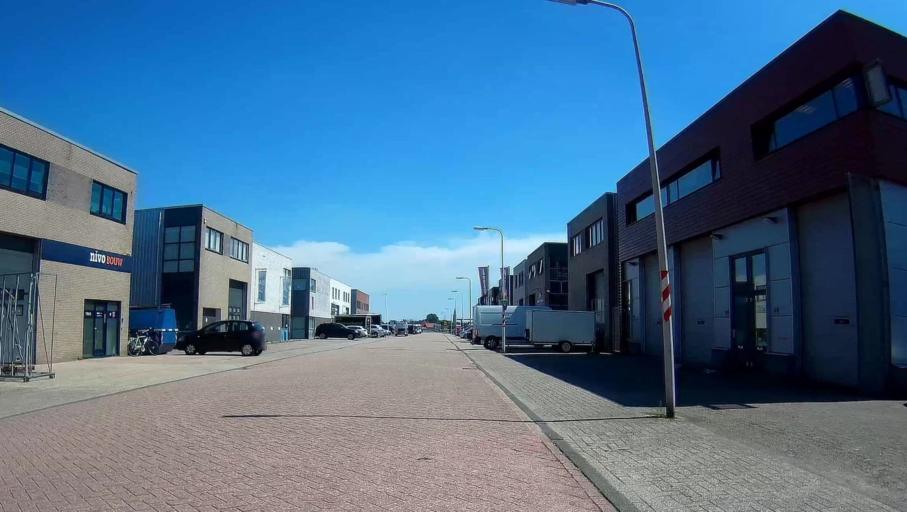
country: NL
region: South Holland
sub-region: Gemeente Westland
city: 's-Gravenzande
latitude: 51.9946
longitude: 4.1796
